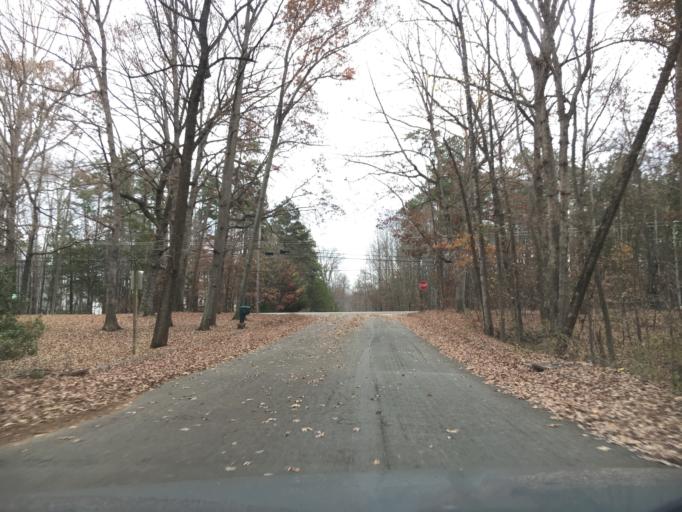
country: US
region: Virginia
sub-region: Halifax County
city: South Boston
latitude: 36.7276
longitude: -78.9072
